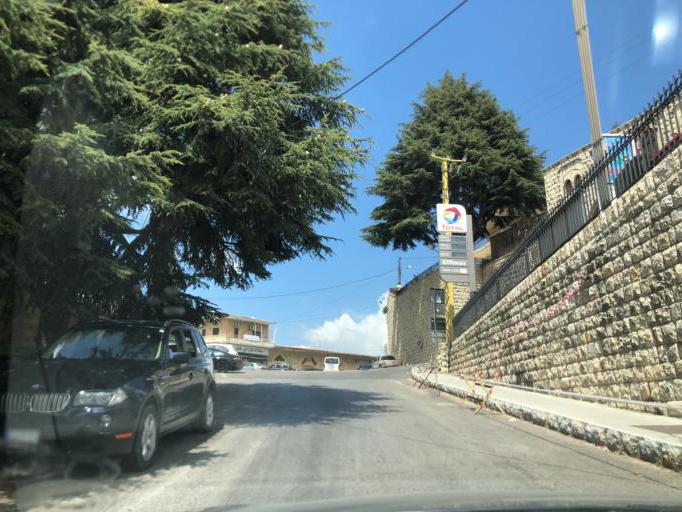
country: LB
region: Mont-Liban
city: Beit ed Dine
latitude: 33.6949
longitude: 35.5810
